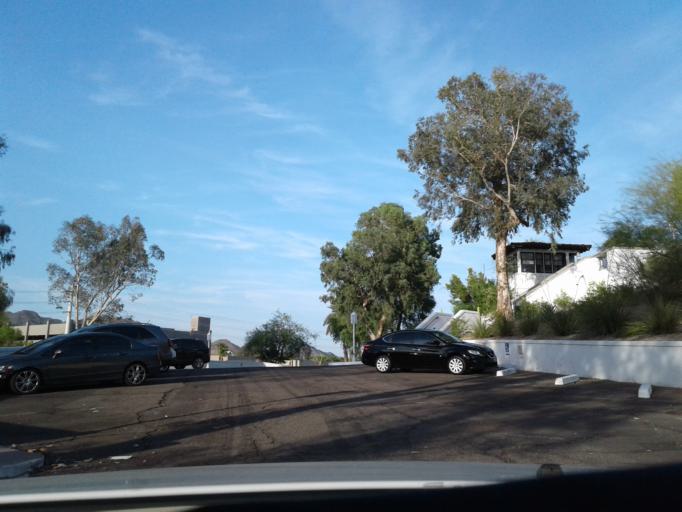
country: US
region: Arizona
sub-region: Maricopa County
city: Paradise Valley
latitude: 33.5234
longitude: -112.0274
